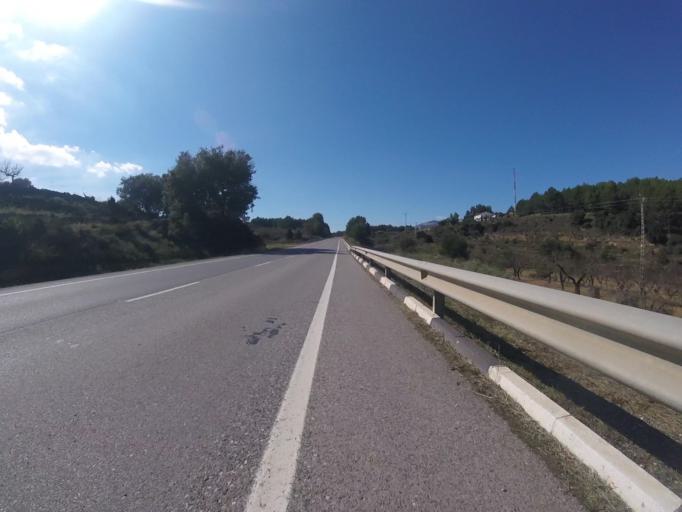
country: ES
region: Valencia
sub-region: Provincia de Castello
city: Sierra-Engarceran
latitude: 40.3229
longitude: -0.0235
